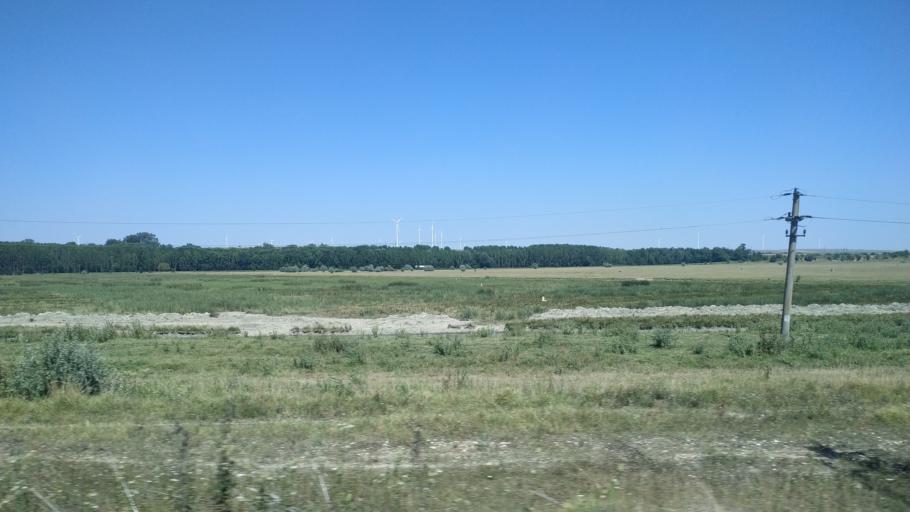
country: RO
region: Constanta
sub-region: Comuna Mircea Voda
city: Mircea Voda
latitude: 44.2646
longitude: 28.1600
